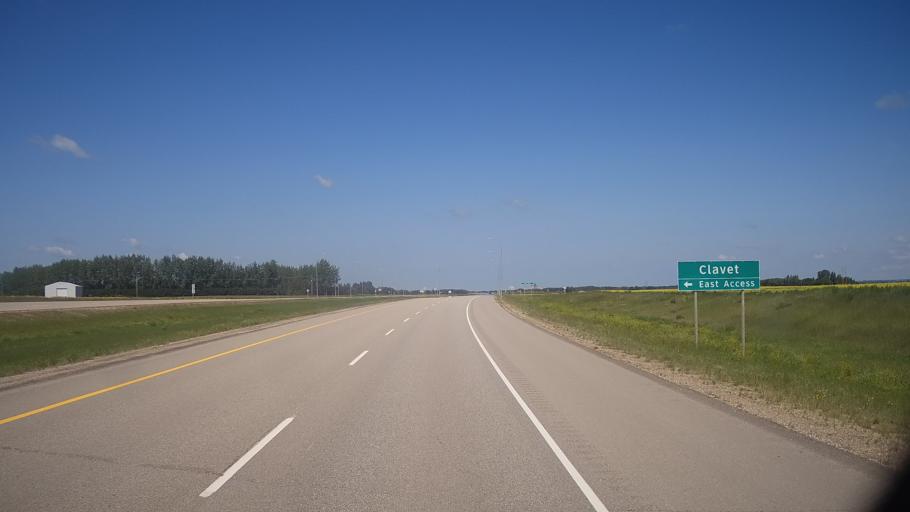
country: CA
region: Saskatchewan
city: Saskatoon
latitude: 51.9996
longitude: -106.3278
